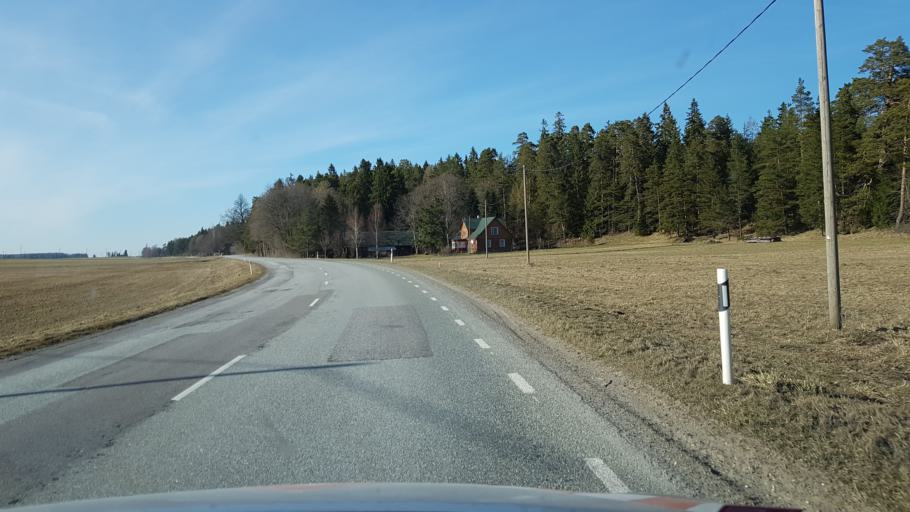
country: EE
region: Laeaene-Virumaa
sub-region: Vinni vald
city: Vinni
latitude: 59.1862
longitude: 26.5757
